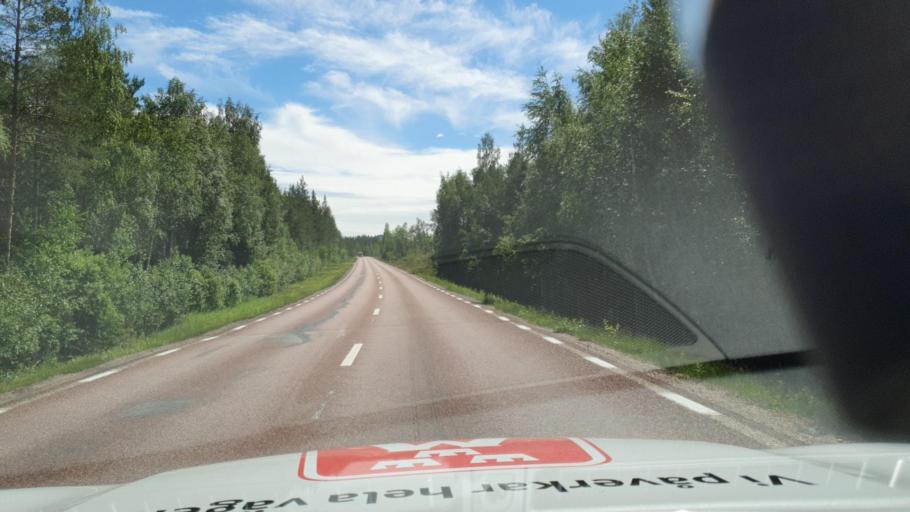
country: SE
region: Jaemtland
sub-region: Harjedalens Kommun
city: Sveg
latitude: 61.9353
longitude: 14.5934
